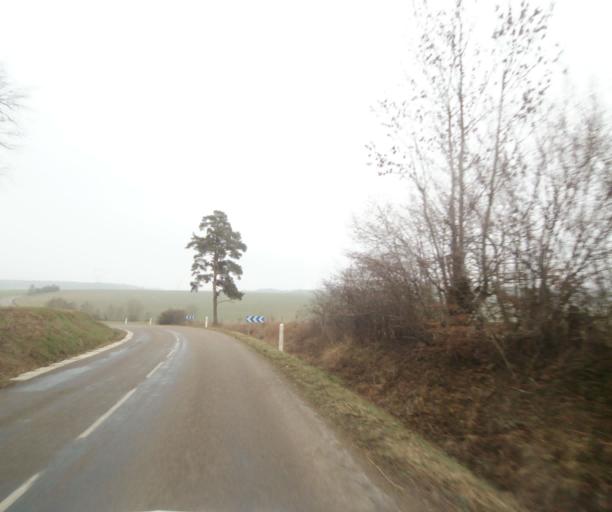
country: FR
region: Champagne-Ardenne
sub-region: Departement de la Haute-Marne
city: Wassy
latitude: 48.5137
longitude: 5.0113
